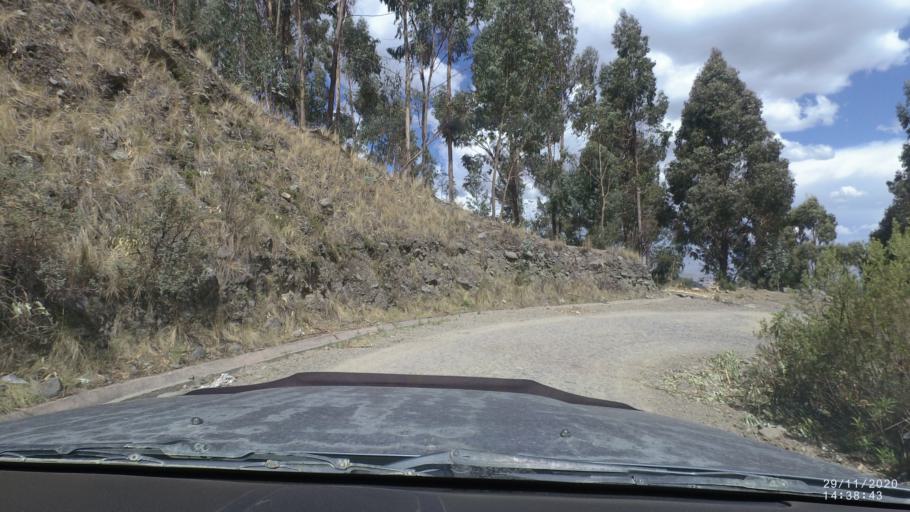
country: BO
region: Cochabamba
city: Sipe Sipe
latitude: -17.2722
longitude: -66.3282
